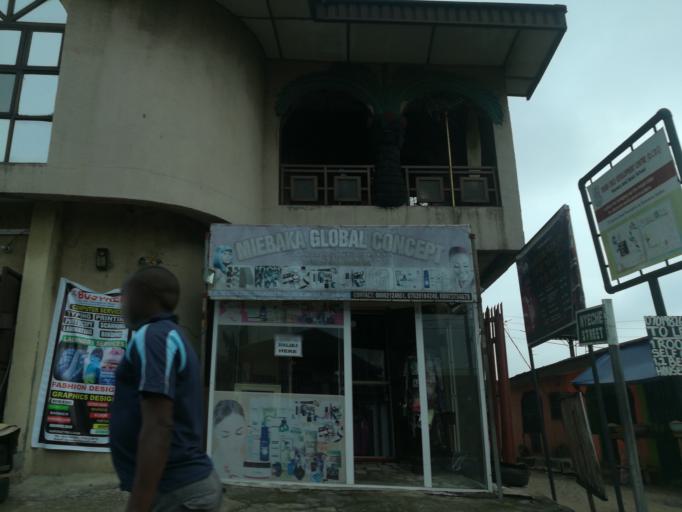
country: NG
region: Rivers
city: Port Harcourt
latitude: 4.8764
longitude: 6.9863
